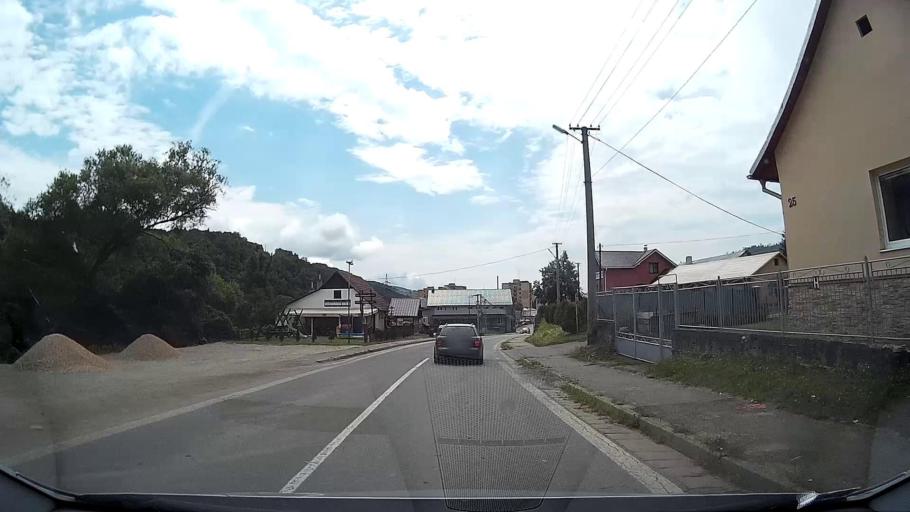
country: SK
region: Banskobystricky
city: Tisovec
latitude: 48.5829
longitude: 19.9534
